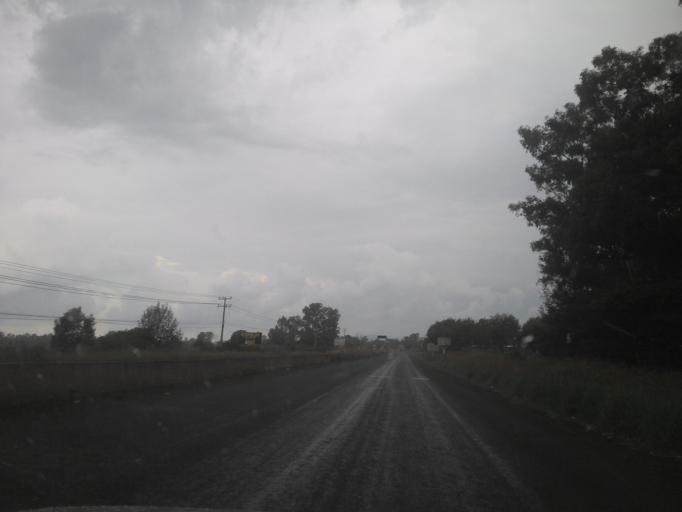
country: MX
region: Jalisco
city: Arandas
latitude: 20.7115
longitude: -102.4120
